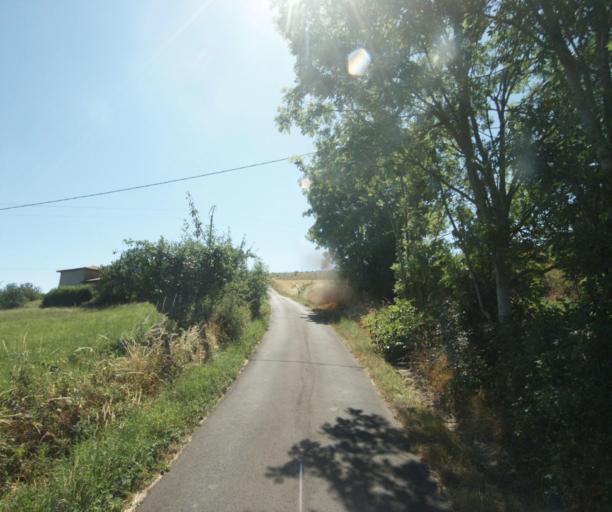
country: FR
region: Rhone-Alpes
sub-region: Departement du Rhone
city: Montrottier
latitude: 45.7862
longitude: 4.5041
